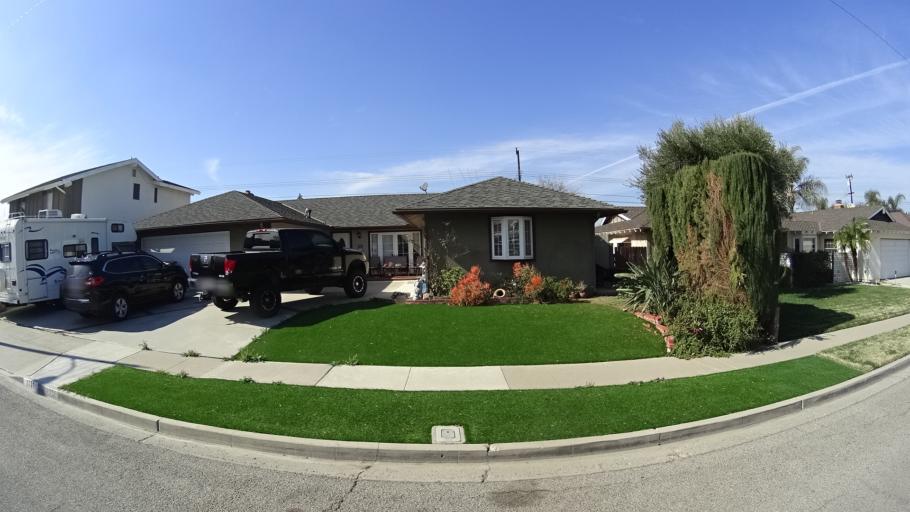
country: US
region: California
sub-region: Orange County
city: Placentia
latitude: 33.8942
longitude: -117.8484
